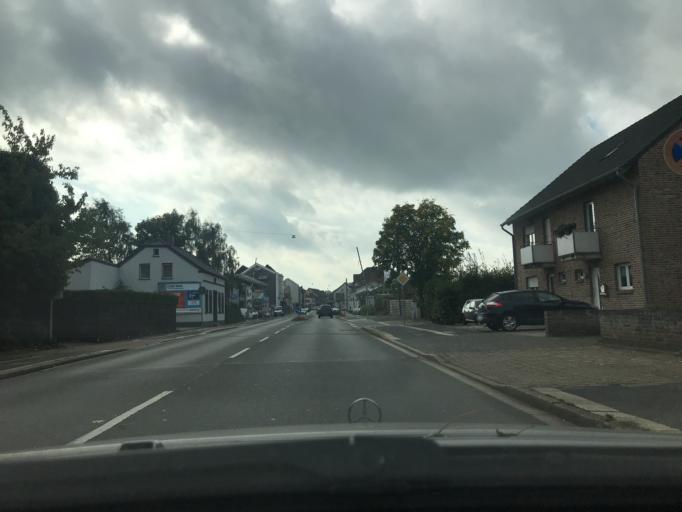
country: DE
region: North Rhine-Westphalia
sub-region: Regierungsbezirk Dusseldorf
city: Moers
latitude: 51.4589
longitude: 6.6299
